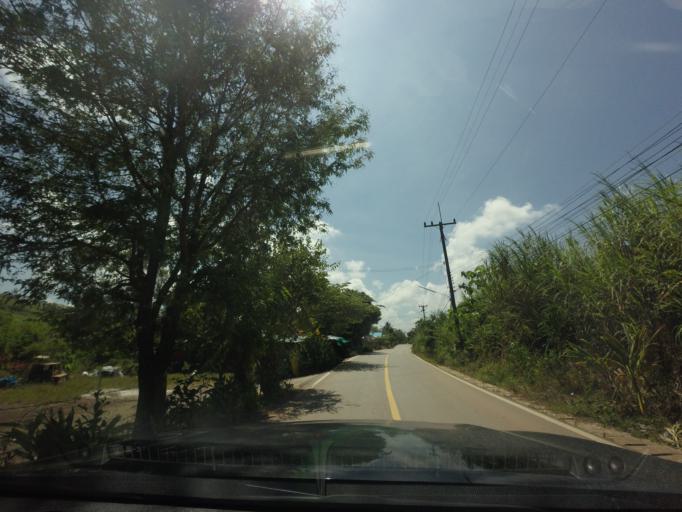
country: TH
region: Phetchabun
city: Khao Kho
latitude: 16.7805
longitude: 101.0477
